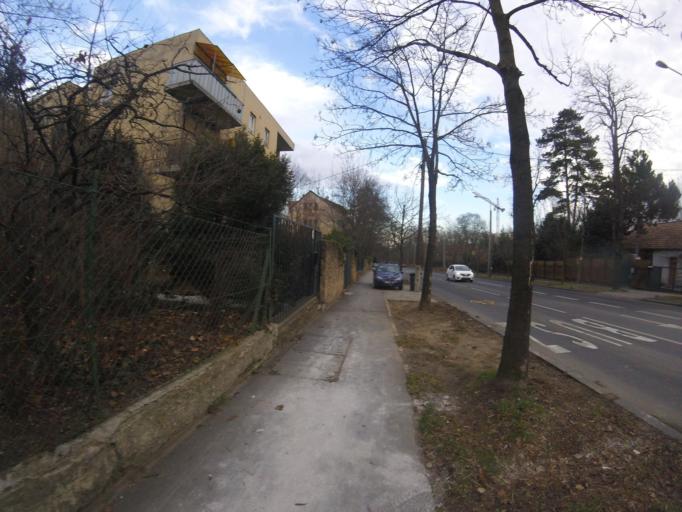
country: HU
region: Budapest
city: Budapest XII. keruelet
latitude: 47.5183
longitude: 18.9865
